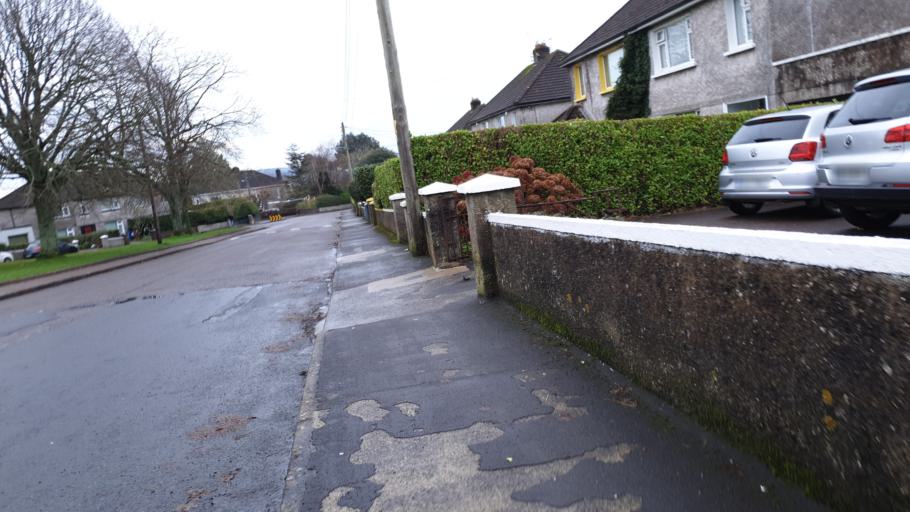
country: IE
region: Munster
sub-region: County Cork
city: Cork
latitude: 51.8892
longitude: -8.4253
